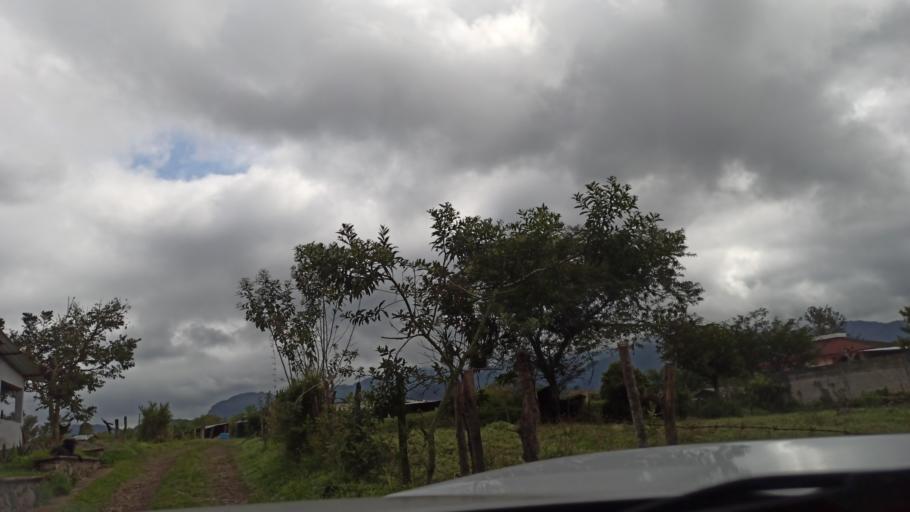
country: MX
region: Veracruz
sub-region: Chocaman
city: San Jose Neria
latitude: 19.0000
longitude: -97.0018
